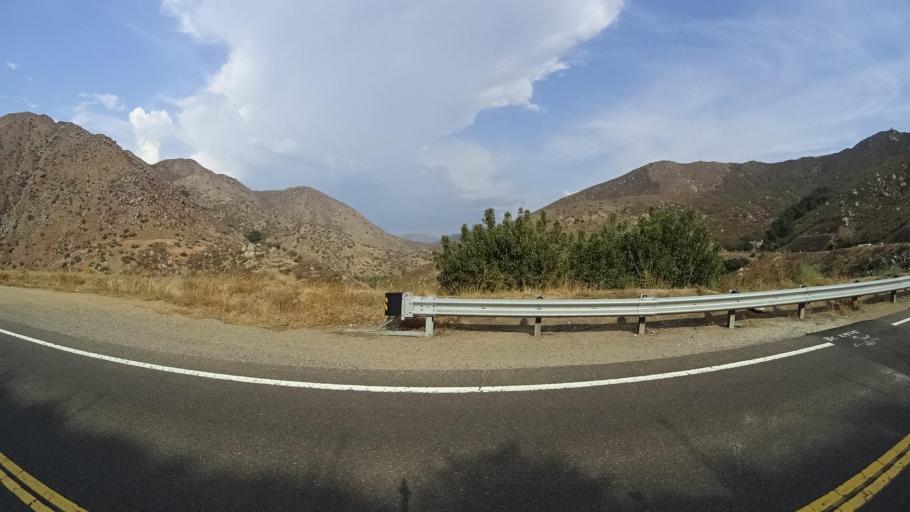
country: US
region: California
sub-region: San Diego County
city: San Pasqual
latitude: 33.0843
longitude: -116.9213
